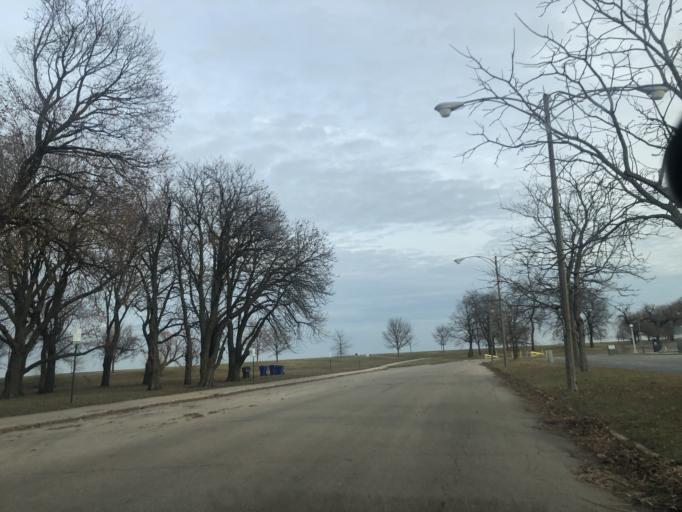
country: US
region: Illinois
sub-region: Cook County
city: Chicago
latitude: 41.9465
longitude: -87.6385
